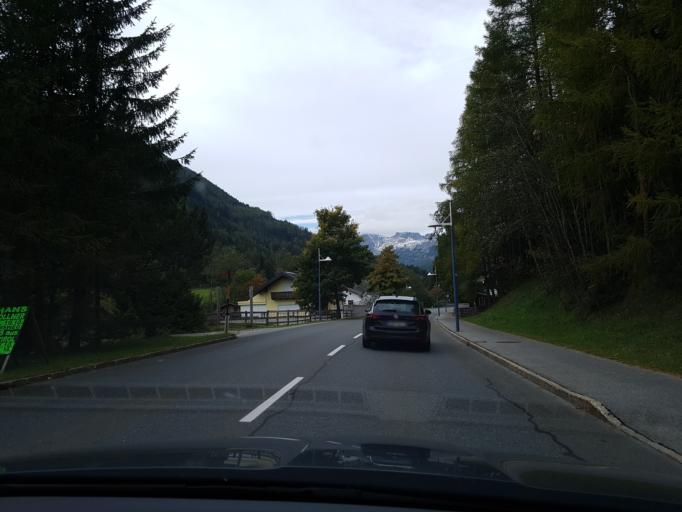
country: AT
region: Salzburg
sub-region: Politischer Bezirk Tamsweg
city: Tweng
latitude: 47.1912
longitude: 13.5993
